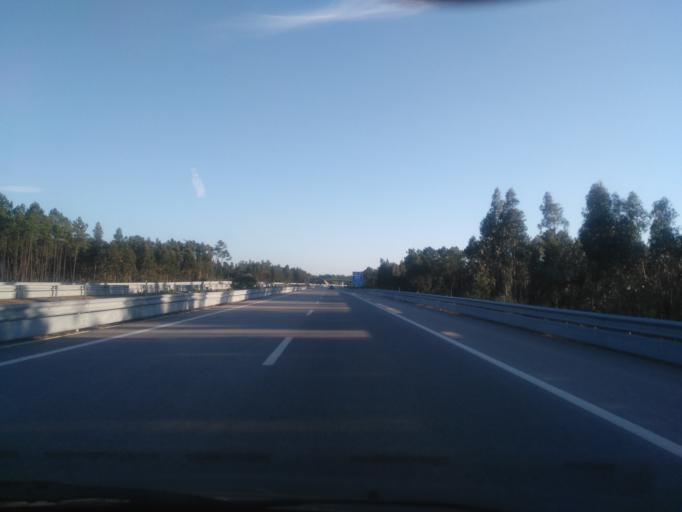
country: PT
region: Coimbra
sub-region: Figueira da Foz
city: Alhadas
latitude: 40.2420
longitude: -8.7838
